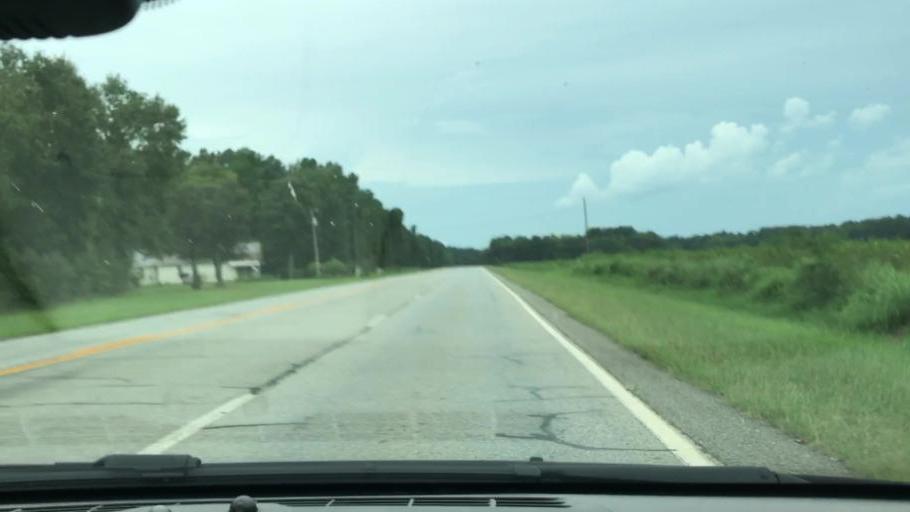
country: US
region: Georgia
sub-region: Early County
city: Blakely
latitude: 31.3382
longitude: -84.9877
